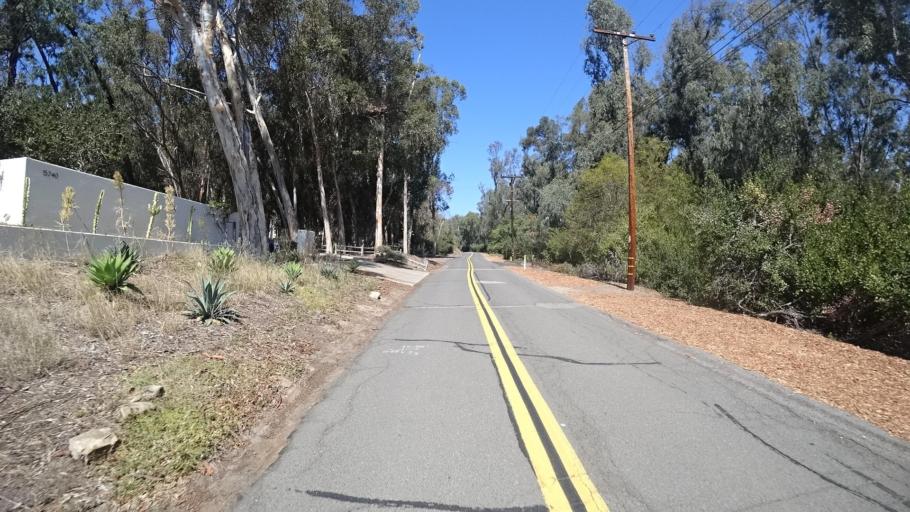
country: US
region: California
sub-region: San Diego County
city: Rancho Santa Fe
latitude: 32.9991
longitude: -117.2149
